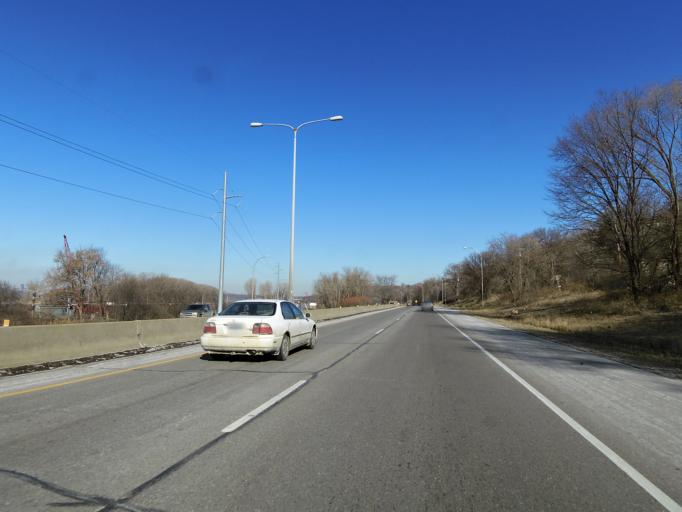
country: US
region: Minnesota
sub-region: Dakota County
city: South Saint Paul
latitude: 44.9229
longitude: -93.0178
